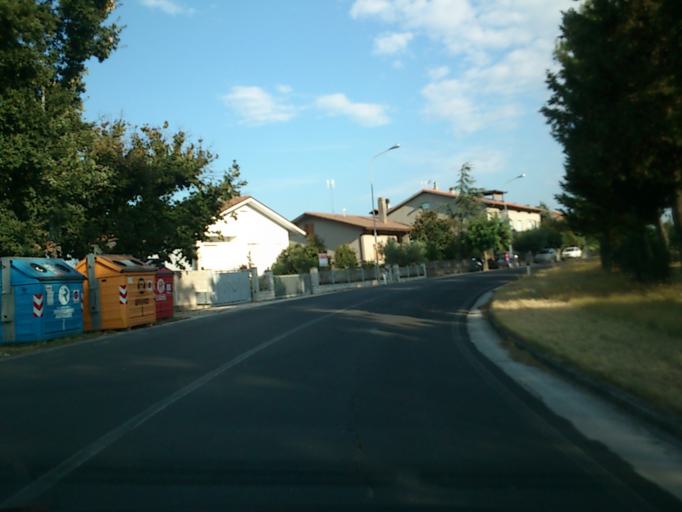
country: IT
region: The Marches
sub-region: Provincia di Pesaro e Urbino
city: San Costanzo
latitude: 43.7799
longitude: 13.0746
